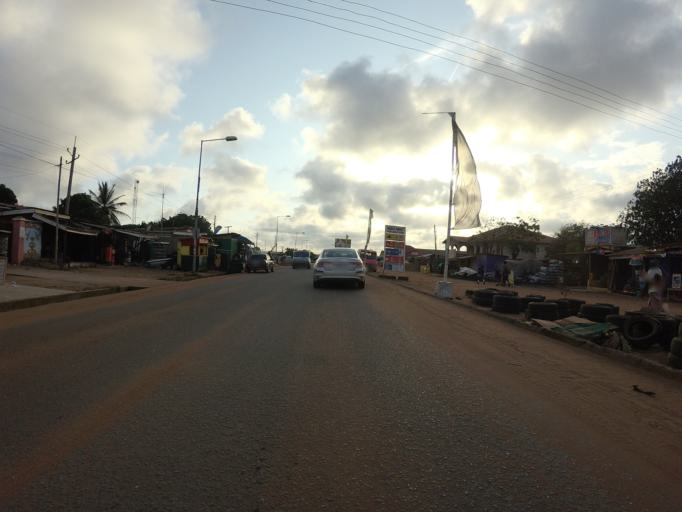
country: GH
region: Greater Accra
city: Teshi Old Town
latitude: 5.6057
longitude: -0.1167
